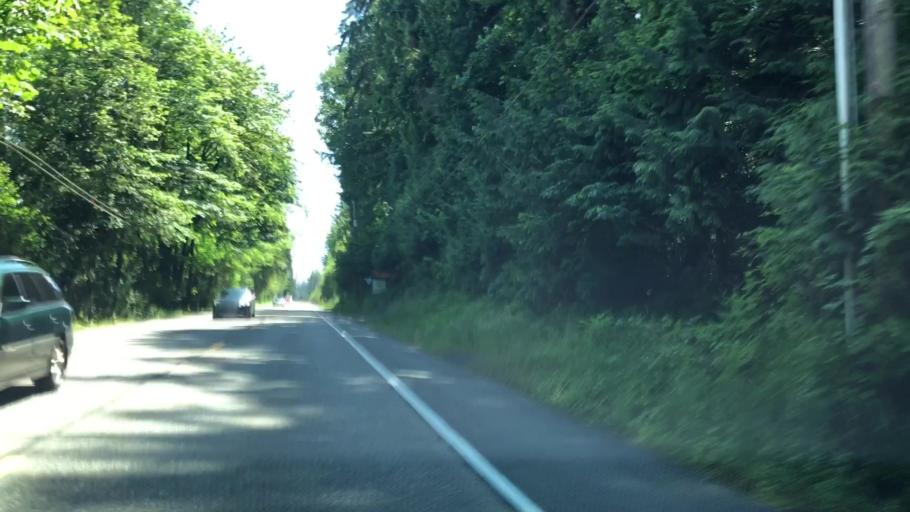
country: US
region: Washington
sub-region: King County
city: Cottage Lake
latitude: 47.7225
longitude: -122.0861
